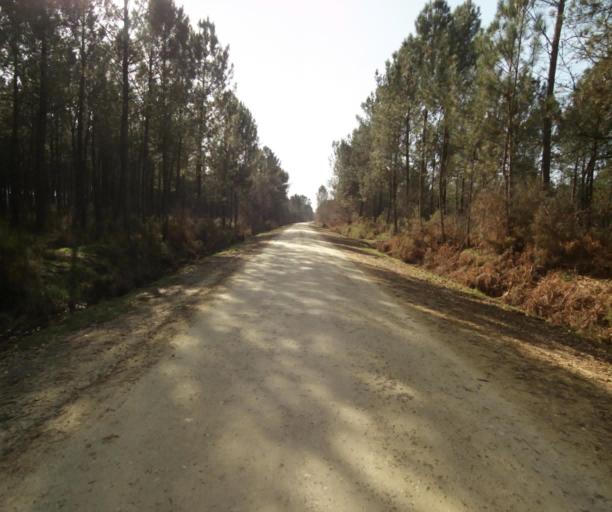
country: FR
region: Aquitaine
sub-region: Departement de la Gironde
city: Grignols
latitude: 44.2197
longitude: -0.1420
